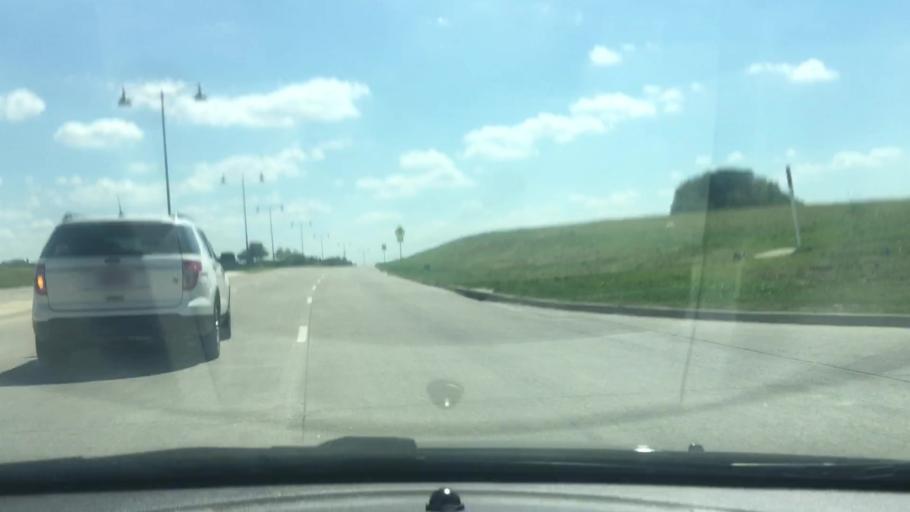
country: US
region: Texas
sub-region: Collin County
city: Prosper
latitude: 33.2333
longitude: -96.7913
